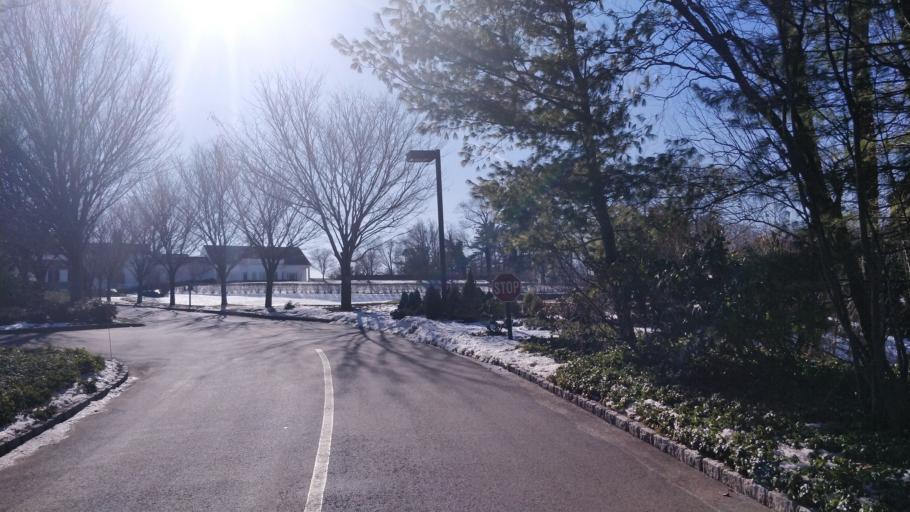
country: US
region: New York
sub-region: Nassau County
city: Old Westbury
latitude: 40.8034
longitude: -73.6017
